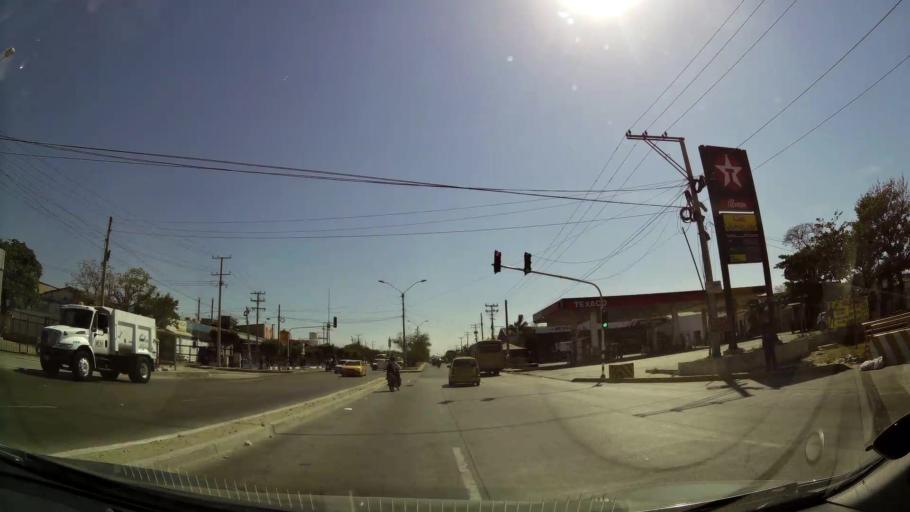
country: CO
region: Atlantico
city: Barranquilla
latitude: 10.9589
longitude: -74.7852
